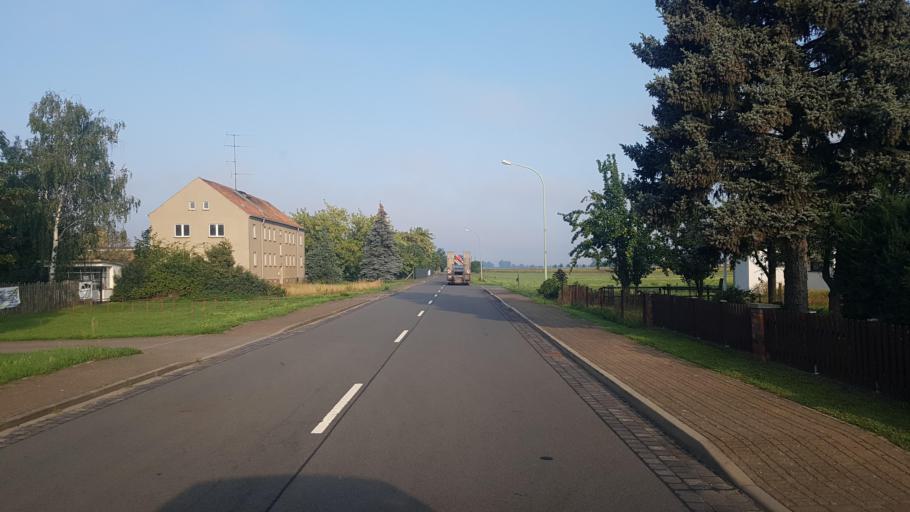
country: DE
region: Saxony-Anhalt
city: Prettin
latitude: 51.7017
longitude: 12.8841
